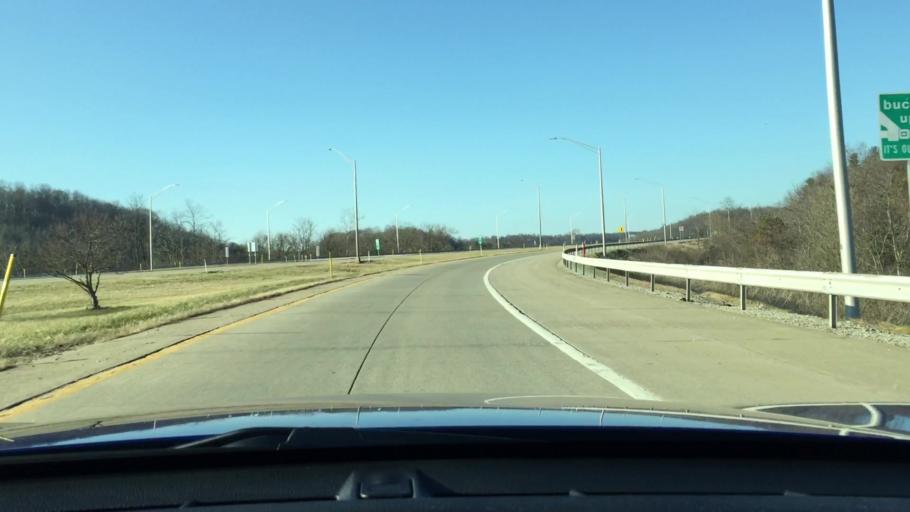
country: US
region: Pennsylvania
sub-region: Westmoreland County
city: New Stanton
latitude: 40.2364
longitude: -79.6032
